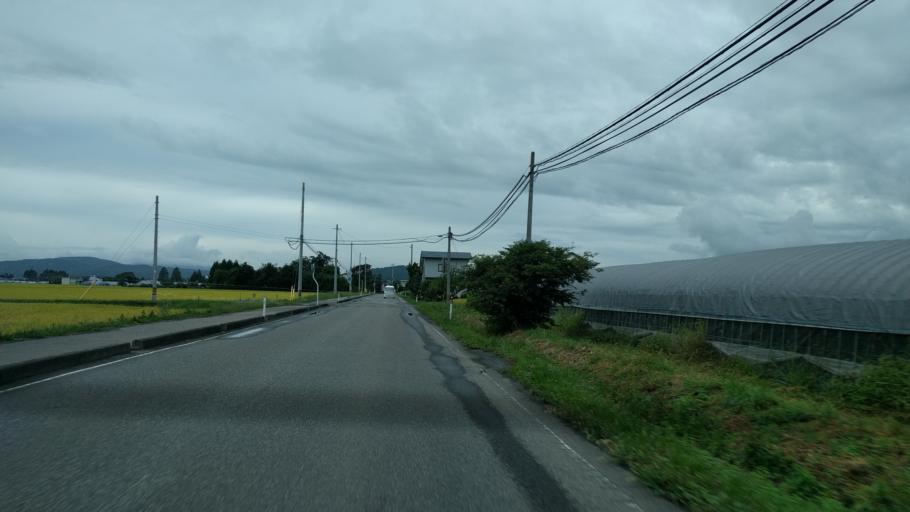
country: JP
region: Fukushima
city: Kitakata
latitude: 37.6096
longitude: 139.8638
